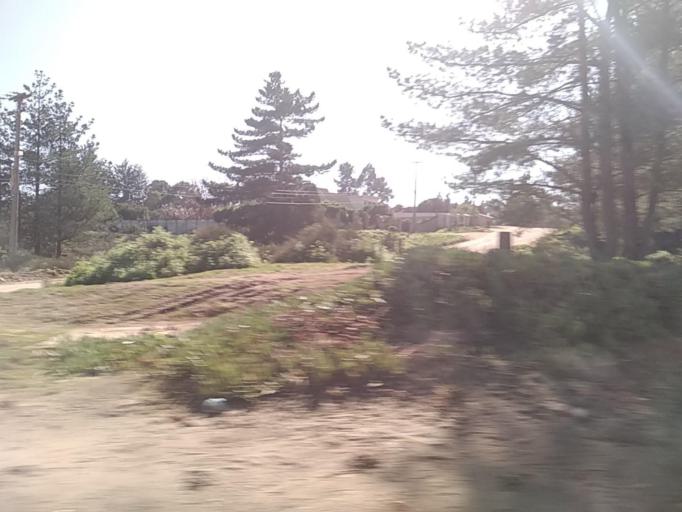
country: CL
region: Valparaiso
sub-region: Provincia de Valparaiso
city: Vina del Mar
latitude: -32.9598
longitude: -71.5305
